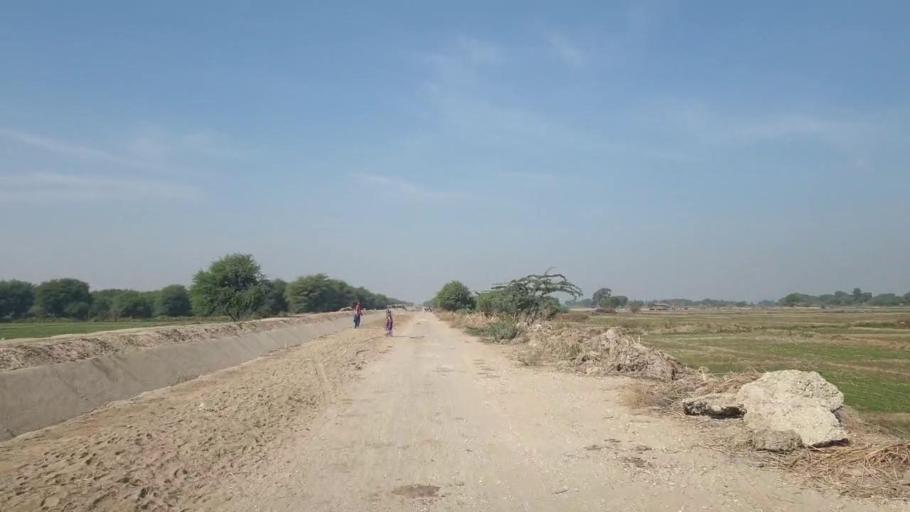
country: PK
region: Sindh
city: Matiari
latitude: 25.6785
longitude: 68.3433
